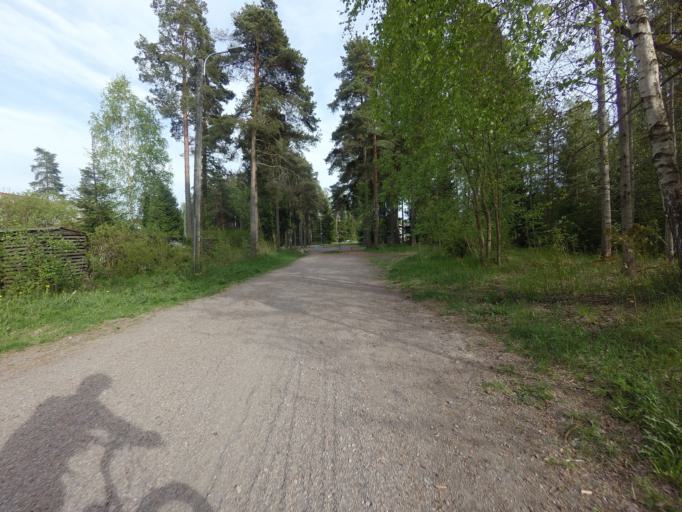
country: FI
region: Uusimaa
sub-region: Helsinki
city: Koukkuniemi
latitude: 60.1449
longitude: 24.6964
